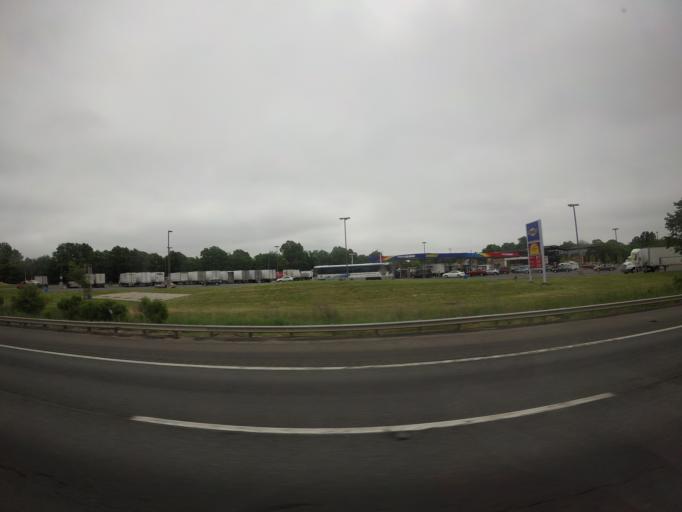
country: US
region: New Jersey
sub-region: Middlesex County
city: Port Reading
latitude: 40.5583
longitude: -74.2635
